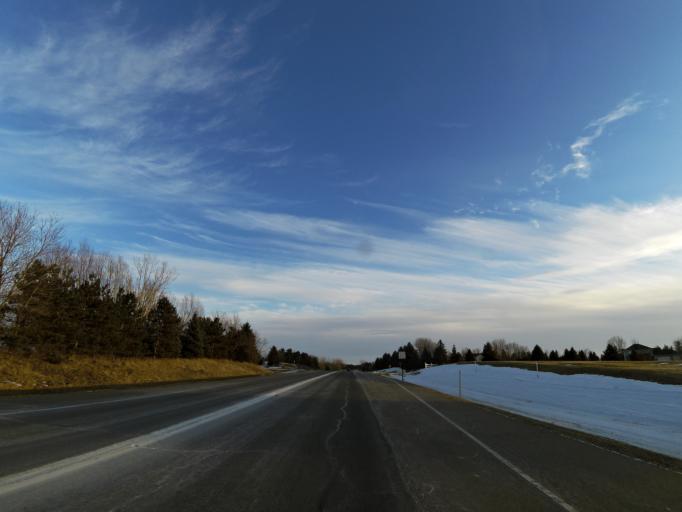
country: US
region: Minnesota
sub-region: Washington County
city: Lake Elmo
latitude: 44.9804
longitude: -92.8601
